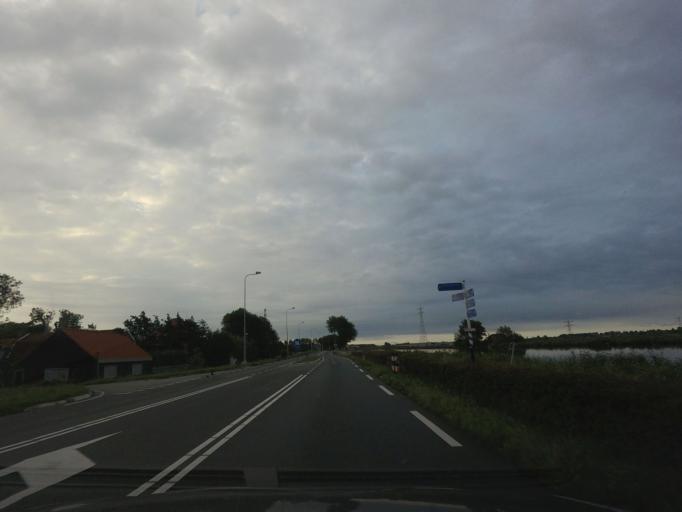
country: NL
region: North Holland
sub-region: Gemeente Uitgeest
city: Uitgeest
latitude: 52.5308
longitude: 4.7784
